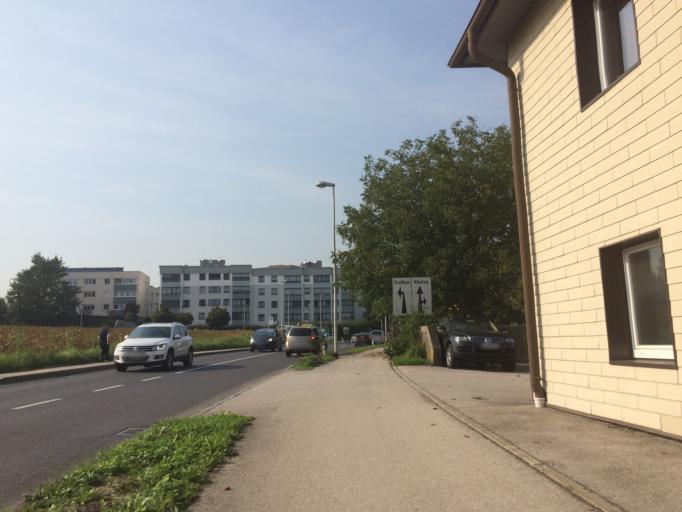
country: AT
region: Upper Austria
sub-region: Politischer Bezirk Linz-Land
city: Leonding
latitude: 48.2779
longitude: 14.2463
